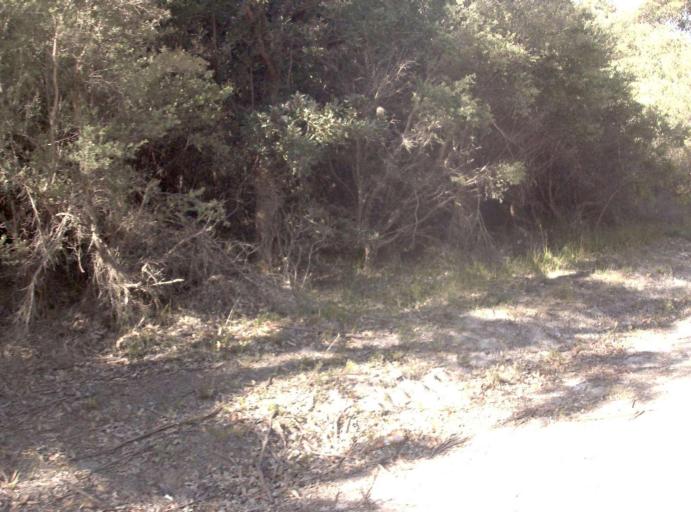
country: AU
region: Victoria
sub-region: East Gippsland
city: Lakes Entrance
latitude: -37.7992
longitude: 148.6712
